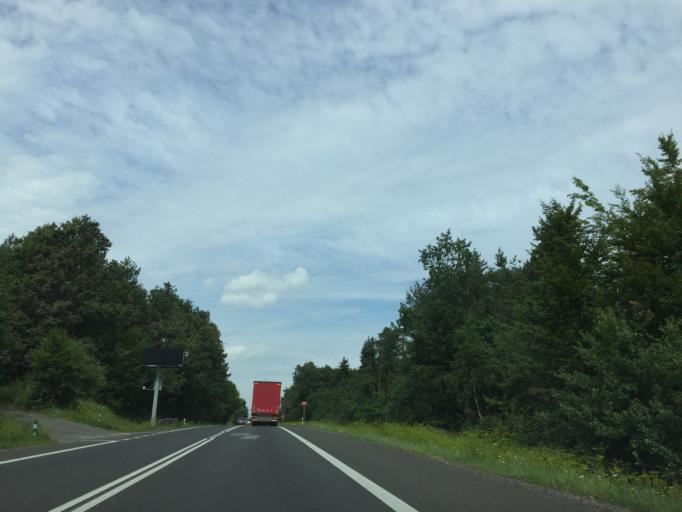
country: PL
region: Lesser Poland Voivodeship
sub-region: Powiat olkuski
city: Osiek
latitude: 50.2620
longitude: 19.6241
